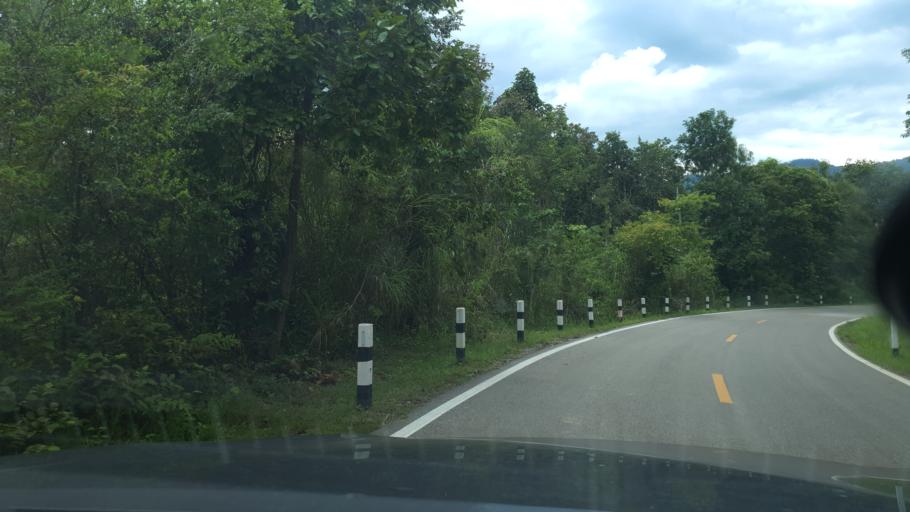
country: TH
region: Lamphun
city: Mae Tha
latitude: 18.5276
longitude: 99.2534
